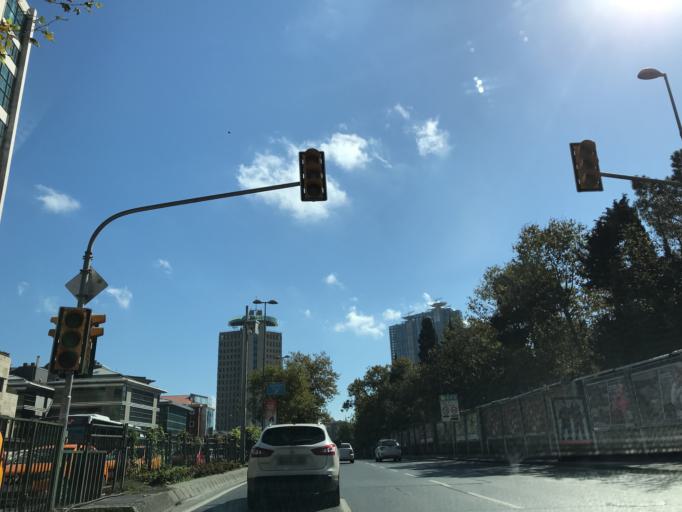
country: TR
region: Istanbul
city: Sisli
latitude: 41.0760
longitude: 29.0145
